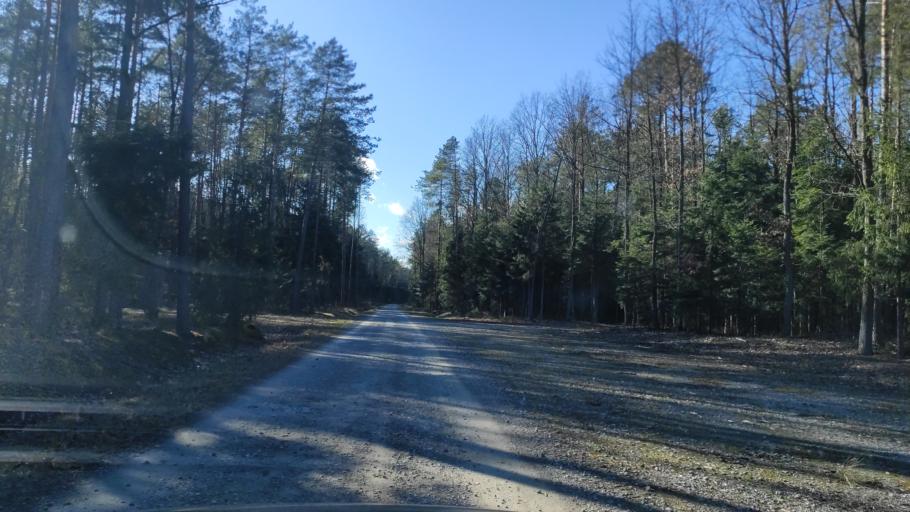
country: PL
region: Masovian Voivodeship
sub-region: Powiat radomski
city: Jastrzebia
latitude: 51.4746
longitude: 21.2779
